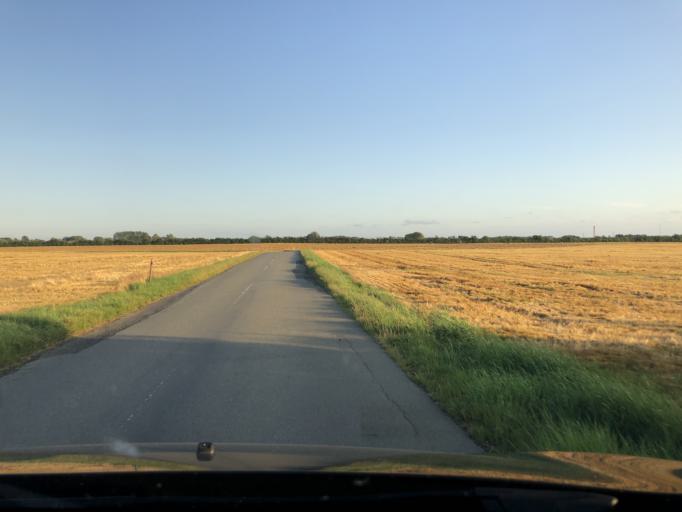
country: DK
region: South Denmark
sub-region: Vejle Kommune
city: Brejning
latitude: 55.6467
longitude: 9.6870
